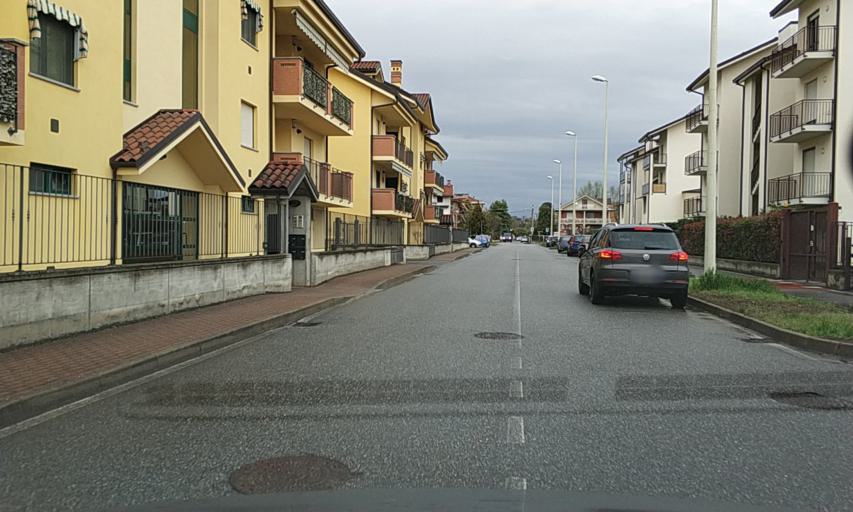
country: IT
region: Piedmont
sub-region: Provincia di Torino
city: Cirie
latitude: 45.2384
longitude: 7.5875
